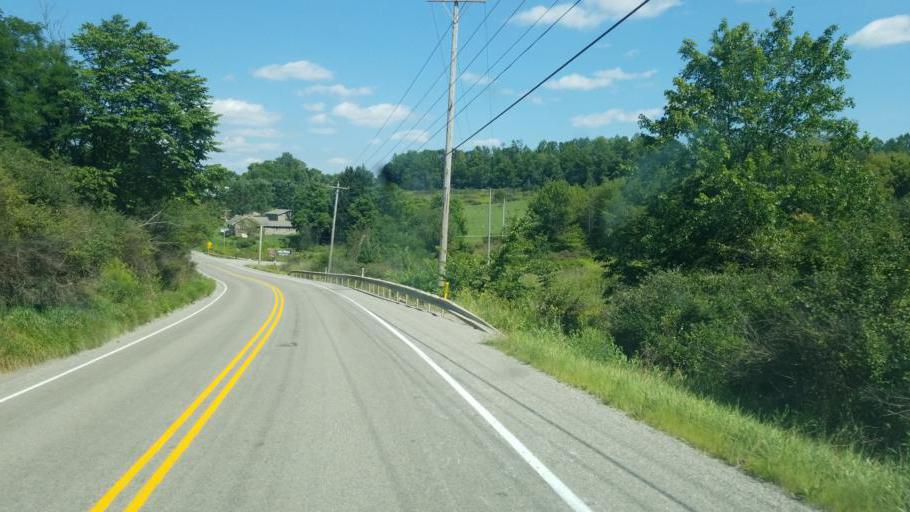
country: US
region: Pennsylvania
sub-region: Clarion County
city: Knox
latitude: 41.1098
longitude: -79.5991
